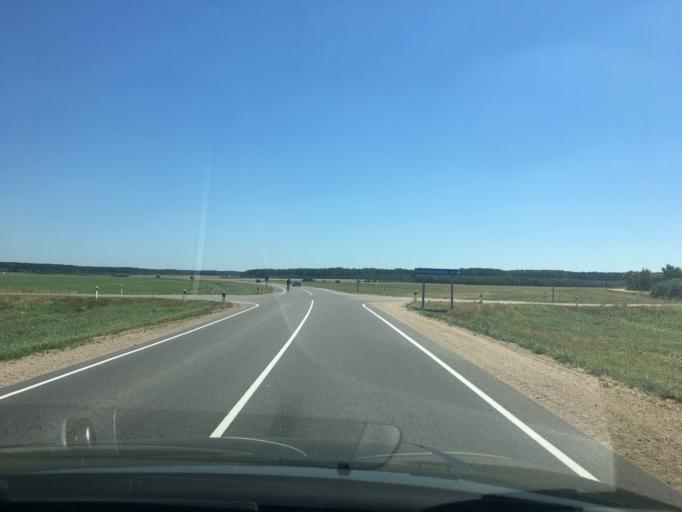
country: BY
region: Grodnenskaya
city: Iwye
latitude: 53.9130
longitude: 25.7727
